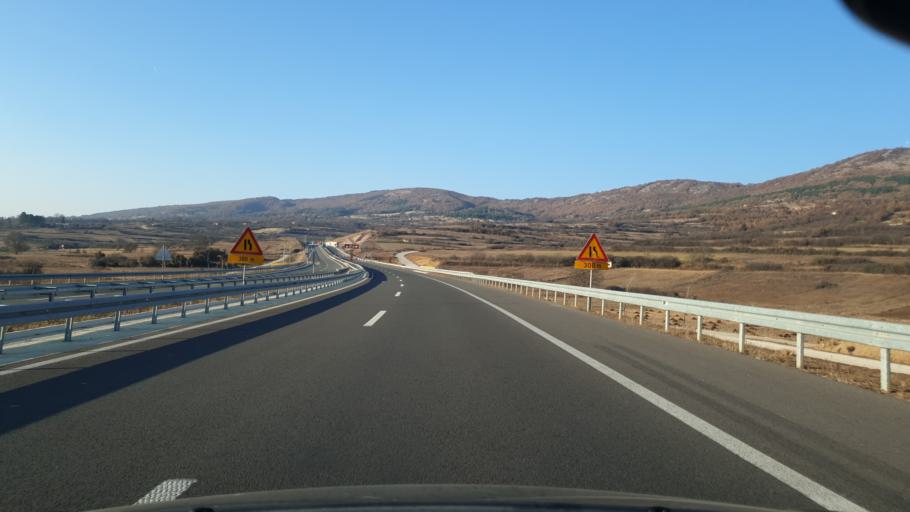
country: RS
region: Central Serbia
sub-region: Pirotski Okrug
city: Dimitrovgrad
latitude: 43.0146
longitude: 22.8020
